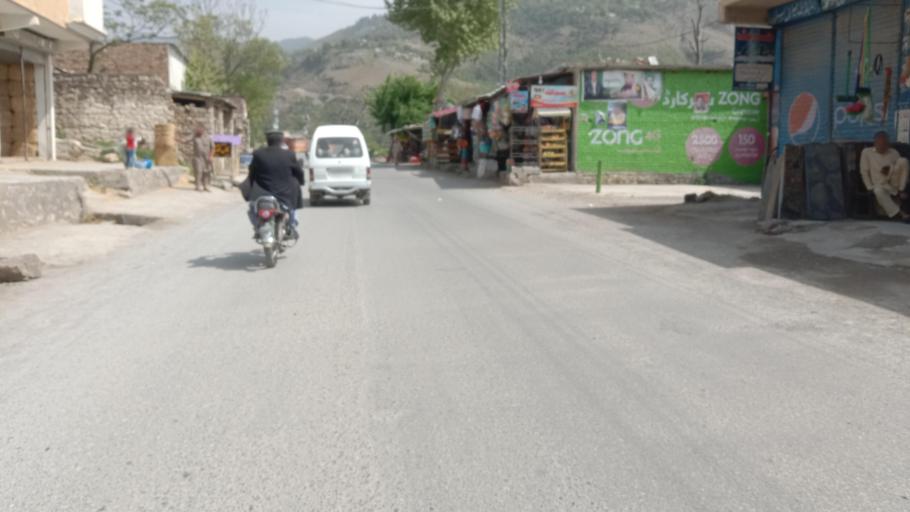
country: PK
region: Khyber Pakhtunkhwa
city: Abbottabad
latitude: 34.1402
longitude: 73.2846
